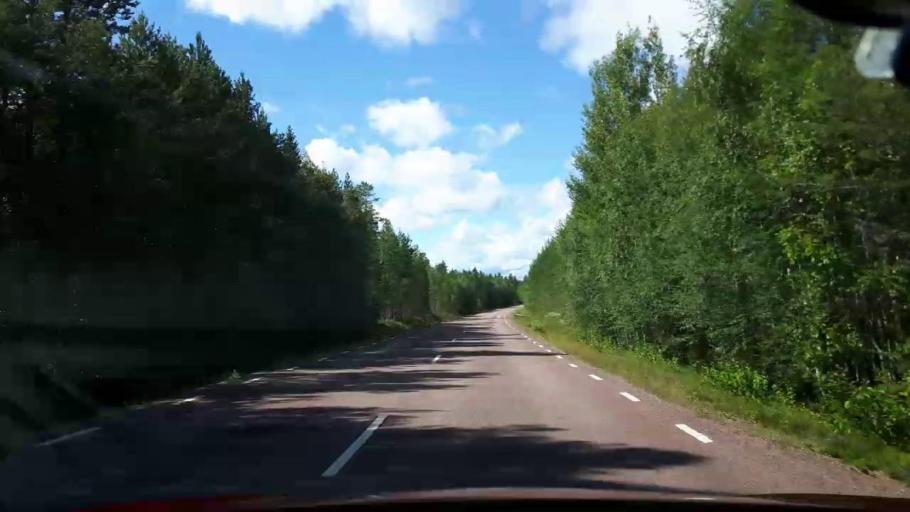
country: SE
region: Jaemtland
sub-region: Harjedalens Kommun
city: Sveg
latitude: 61.9988
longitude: 14.2602
